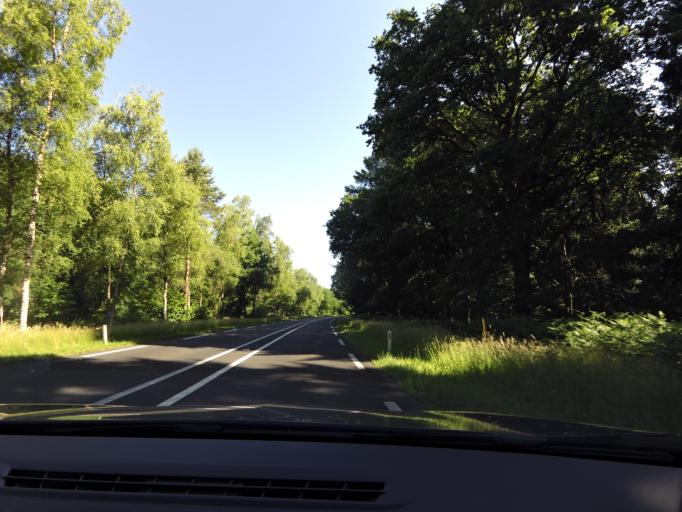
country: NL
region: Overijssel
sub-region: Gemeente Twenterand
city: Den Ham
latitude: 52.4728
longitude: 6.4271
